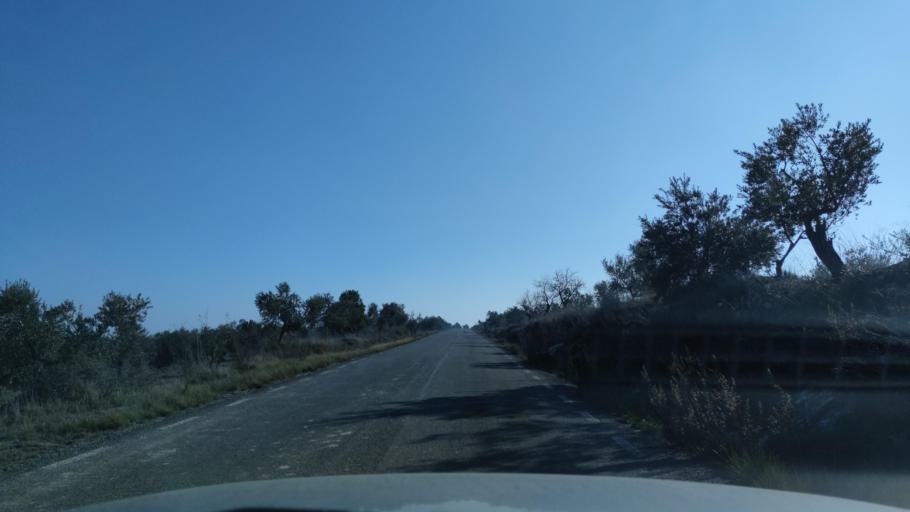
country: ES
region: Catalonia
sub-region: Provincia de Lleida
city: Torrebesses
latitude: 41.4394
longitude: 0.5608
